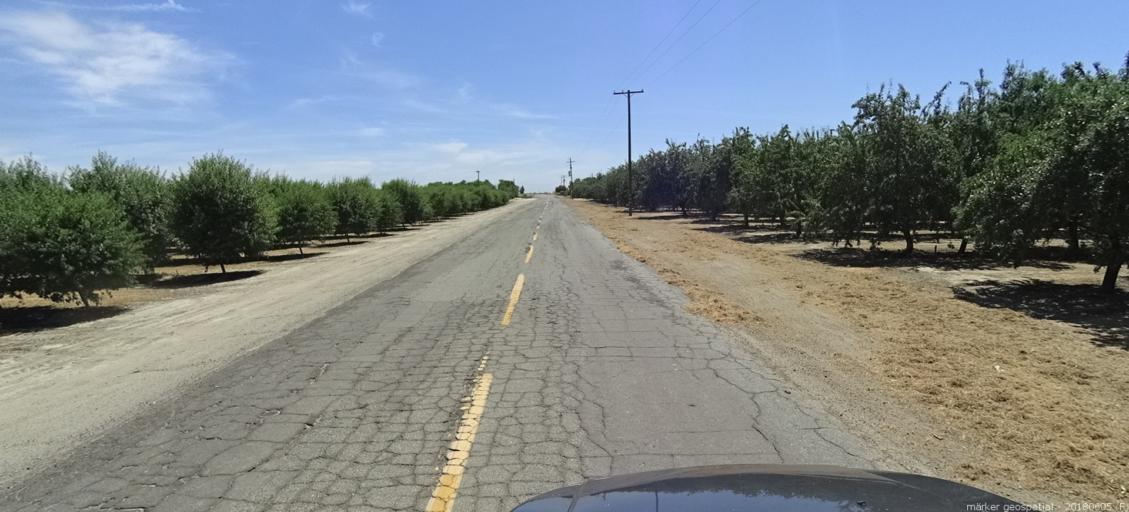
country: US
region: California
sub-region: Madera County
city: Chowchilla
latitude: 37.0545
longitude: -120.4212
